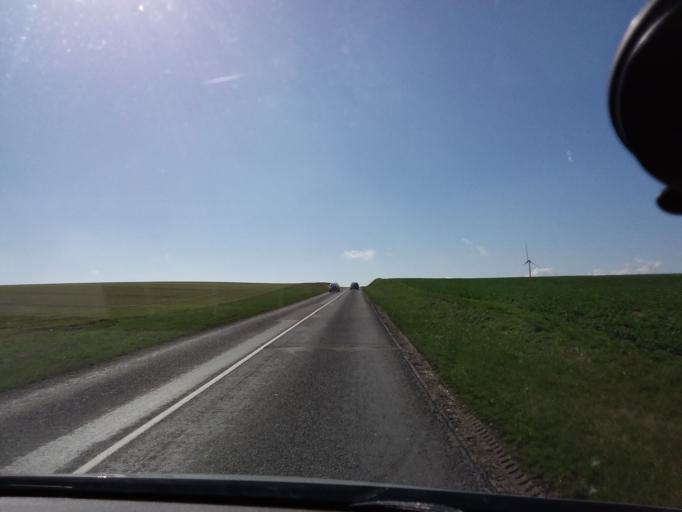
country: FR
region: Picardie
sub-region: Departement de l'Aisne
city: Guignicourt
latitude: 49.5229
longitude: 4.0436
